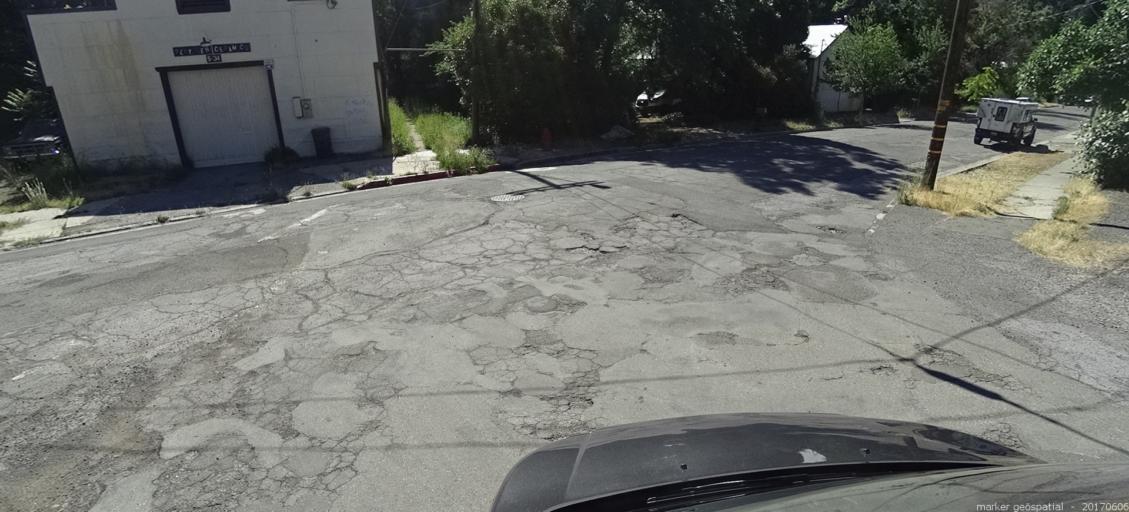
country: US
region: California
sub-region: Siskiyou County
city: Dunsmuir
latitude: 41.2083
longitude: -122.2713
